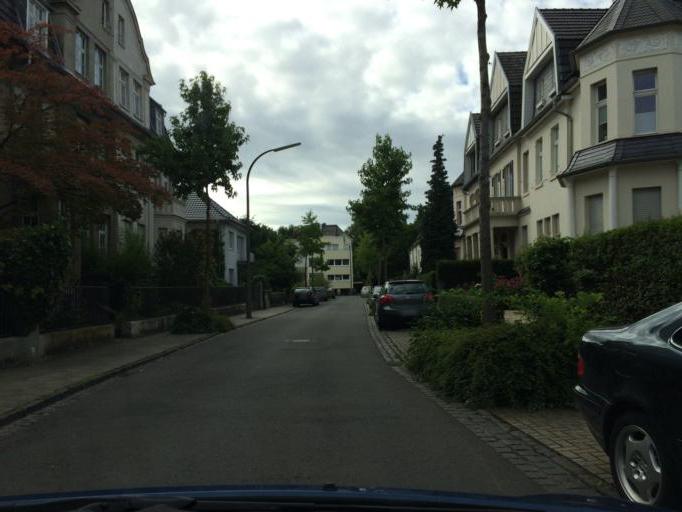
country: DE
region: North Rhine-Westphalia
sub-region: Regierungsbezirk Koln
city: Konigswinter
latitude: 50.6888
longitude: 7.1611
